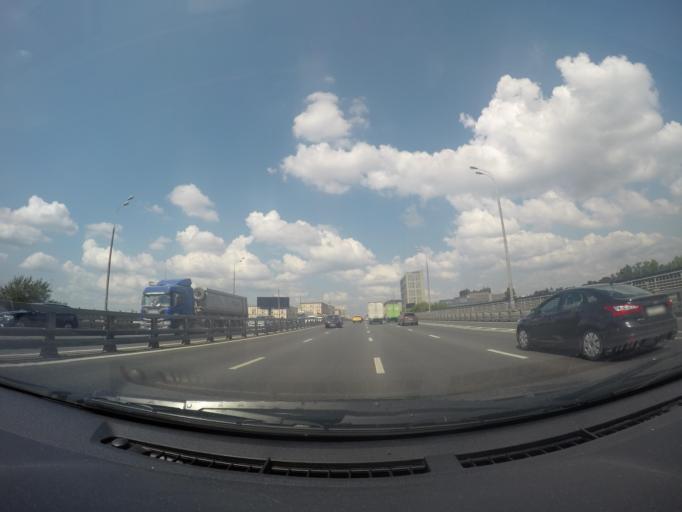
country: RU
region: Moscow
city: Mar'ina Roshcha
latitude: 55.7974
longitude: 37.6351
